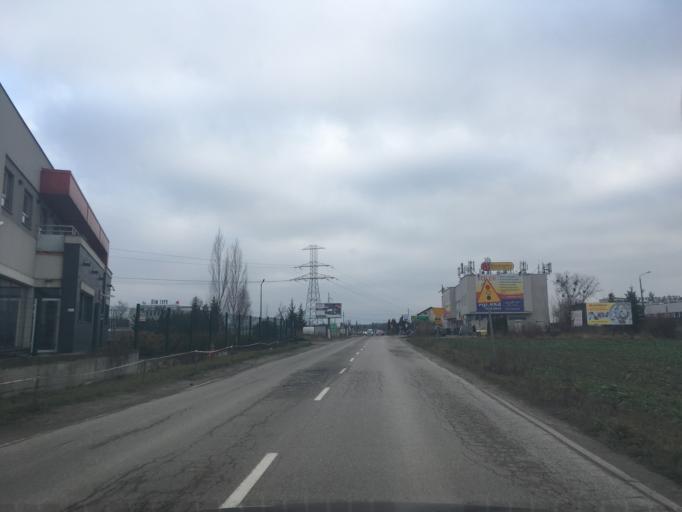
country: PL
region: Masovian Voivodeship
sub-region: Powiat piaseczynski
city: Lesznowola
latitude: 52.0832
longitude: 20.9684
